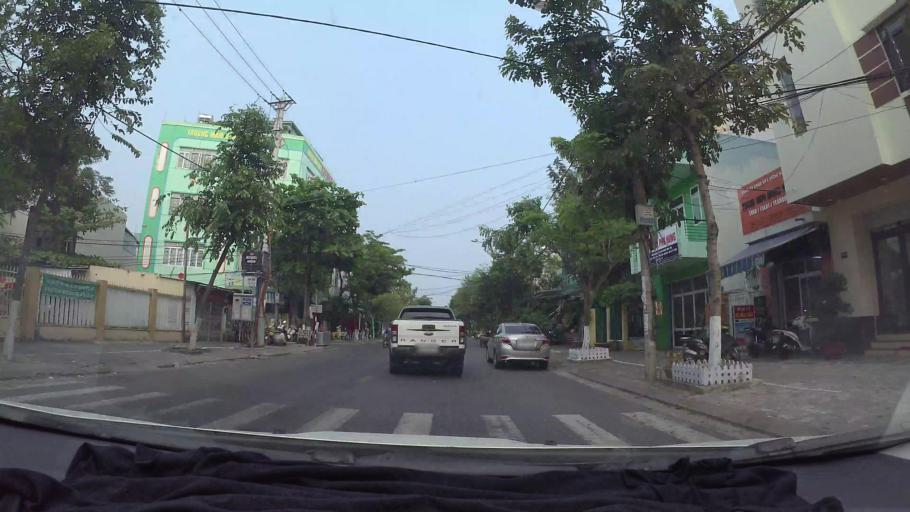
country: VN
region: Da Nang
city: Da Nang
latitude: 16.0441
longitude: 108.2109
